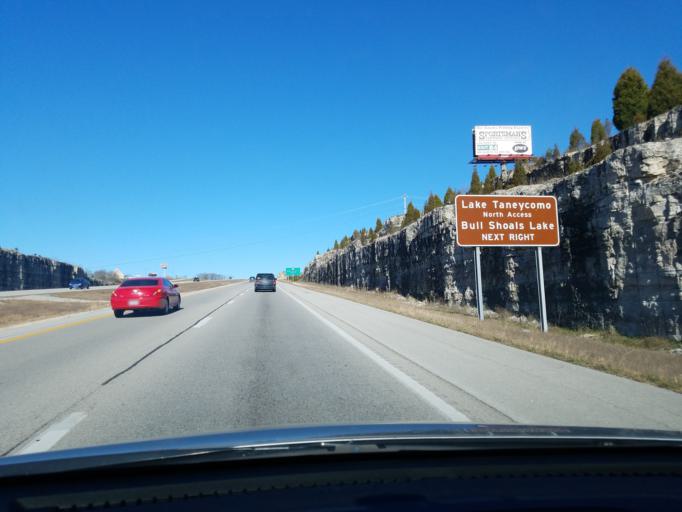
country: US
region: Missouri
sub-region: Taney County
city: Merriam Woods
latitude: 36.7416
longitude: -93.2218
